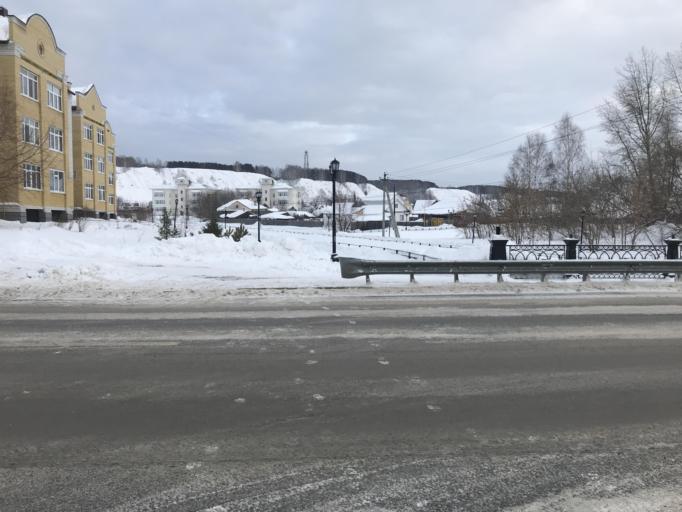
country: RU
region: Tjumen
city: Tobol'sk
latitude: 58.1955
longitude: 68.2490
